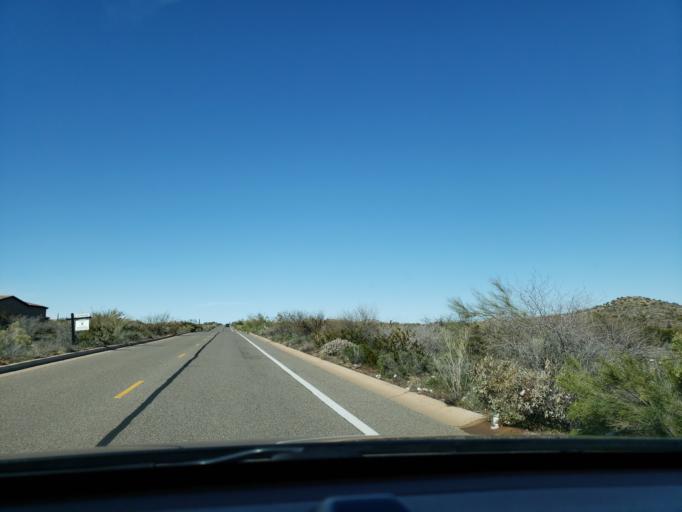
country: US
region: Arizona
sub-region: Maricopa County
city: Carefree
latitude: 33.7178
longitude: -111.8264
